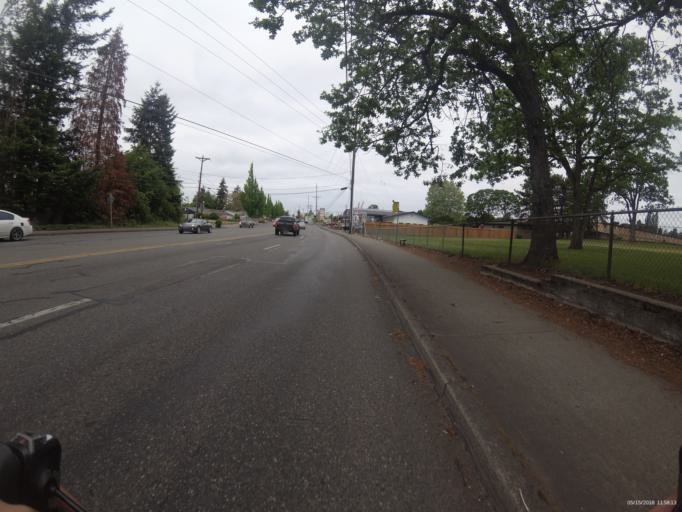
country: US
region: Washington
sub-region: Pierce County
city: Lakewood
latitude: 47.1799
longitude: -122.5417
